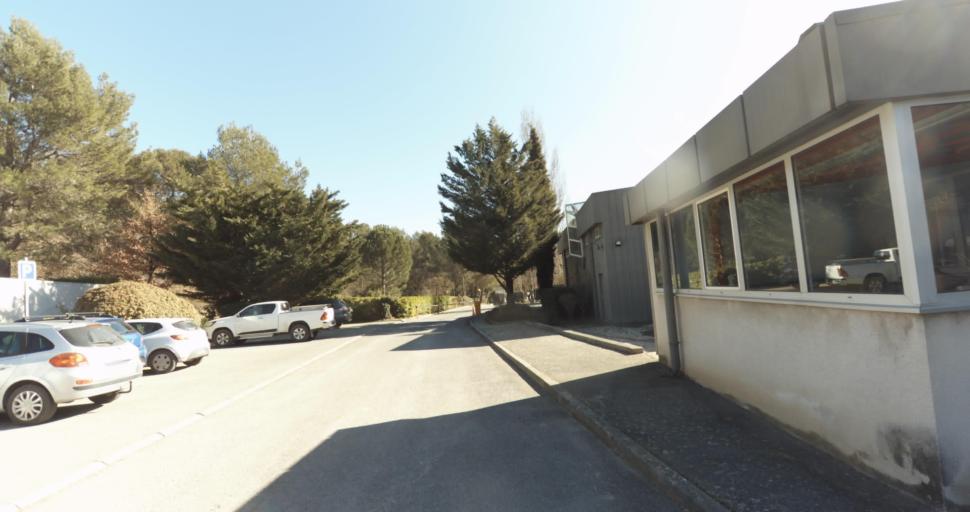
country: FR
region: Provence-Alpes-Cote d'Azur
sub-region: Departement des Bouches-du-Rhone
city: Cadolive
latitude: 43.3926
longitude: 5.5538
